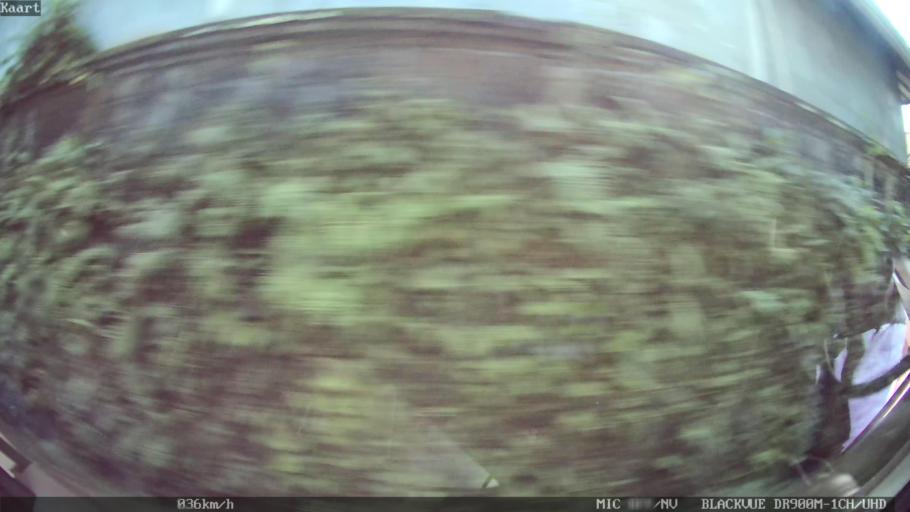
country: ID
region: Bali
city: Banjar Sedang
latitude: -8.5615
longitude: 115.2687
